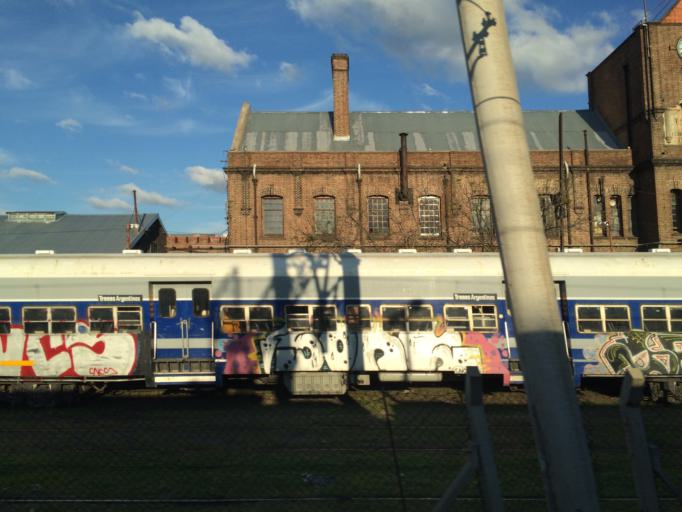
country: AR
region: Buenos Aires
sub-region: Partido de Lanus
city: Lanus
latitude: -34.7274
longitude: -58.3935
